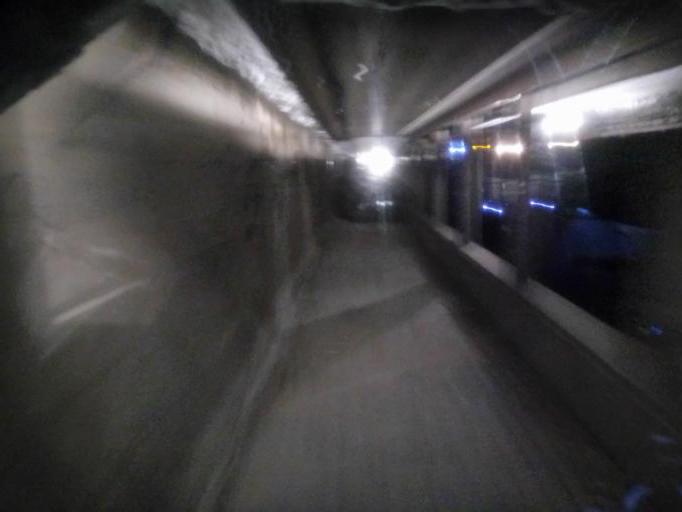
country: FR
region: Rhone-Alpes
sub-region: Departement de la Savoie
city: Saint-Michel-de-Maurienne
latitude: 45.2077
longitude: 6.5341
